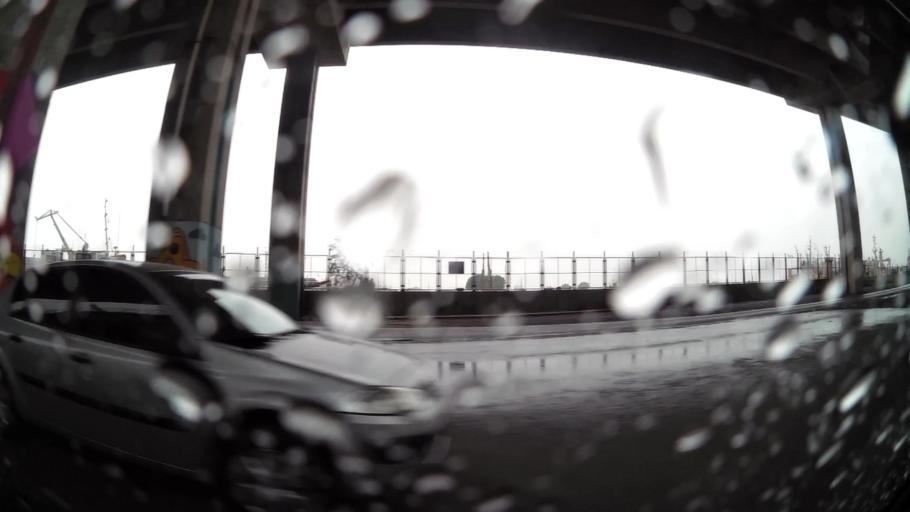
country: AR
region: Buenos Aires F.D.
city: Buenos Aires
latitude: -34.6323
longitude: -58.3537
